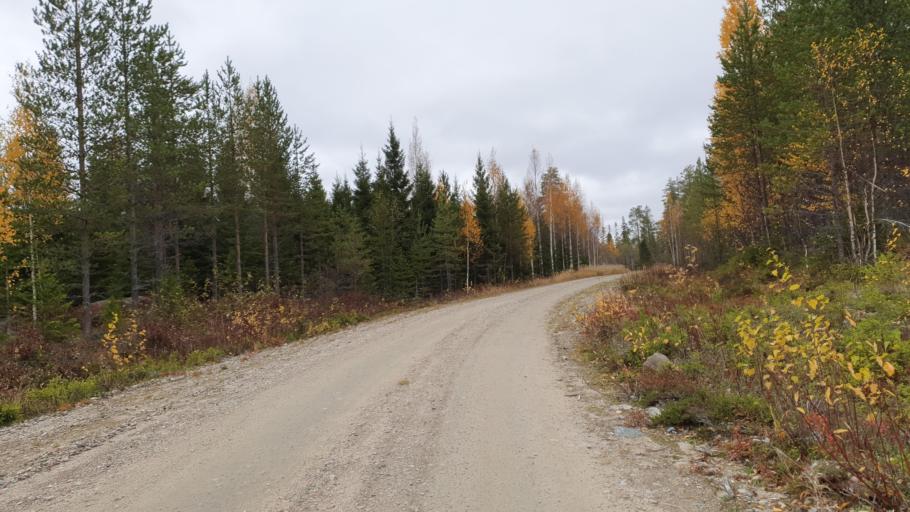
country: FI
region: Kainuu
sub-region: Kehys-Kainuu
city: Kuhmo
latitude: 64.4589
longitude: 29.6059
